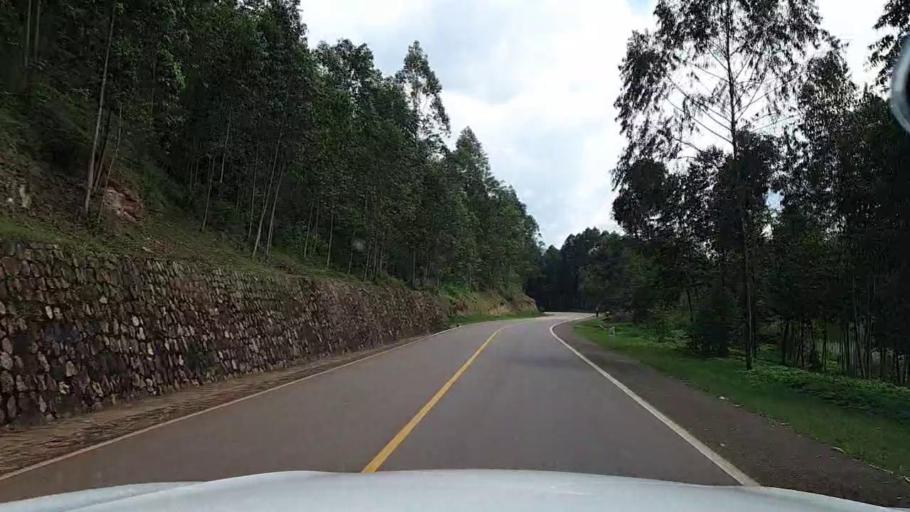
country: RW
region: Kigali
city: Kigali
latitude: -1.8201
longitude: 30.0869
